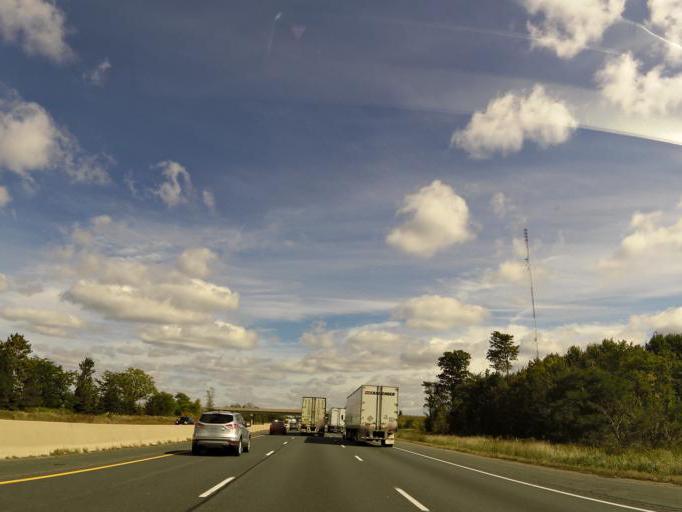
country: CA
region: Ontario
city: Dorchester
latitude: 42.9417
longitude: -81.1386
